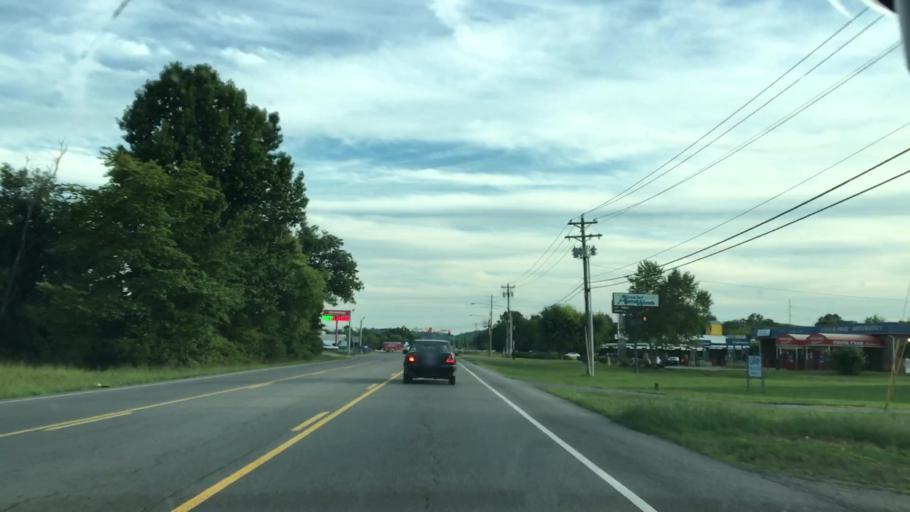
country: US
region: Tennessee
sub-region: Wilson County
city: Lebanon
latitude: 36.1759
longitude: -86.3019
